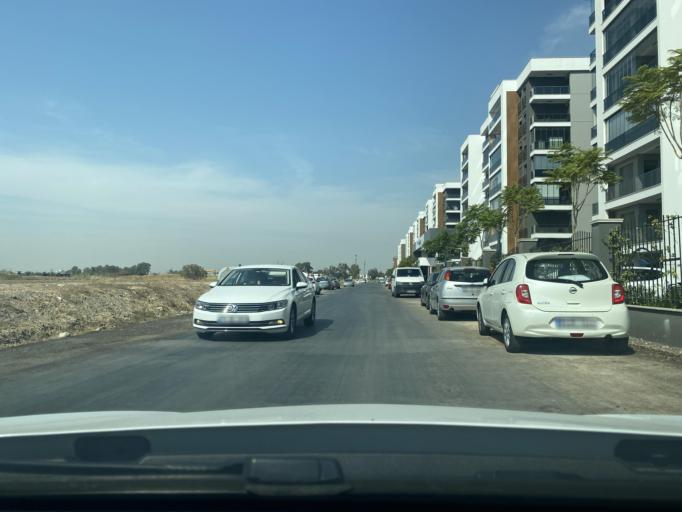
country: TR
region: Izmir
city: Karsiyaka
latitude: 38.4893
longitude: 27.0498
